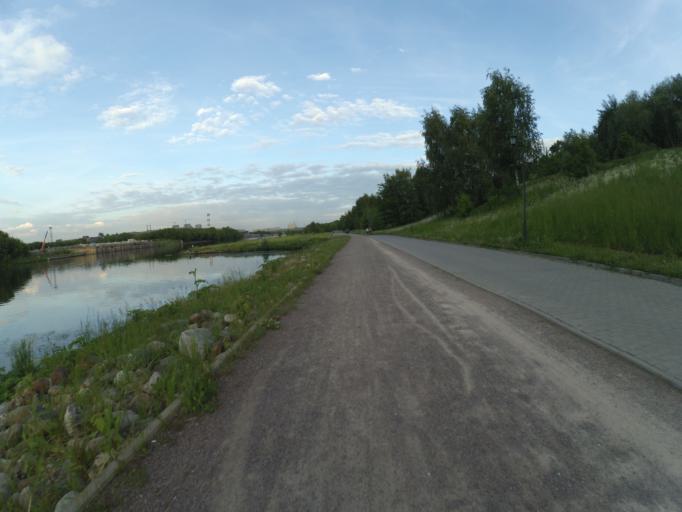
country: RU
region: Moscow
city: Kolomenskoye
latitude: 55.6499
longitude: 37.6762
